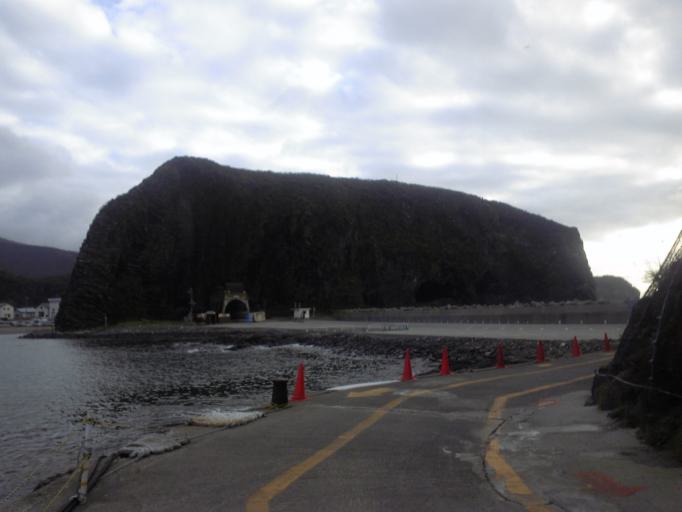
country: JP
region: Hokkaido
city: Shibetsu
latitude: 44.0757
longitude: 144.9919
